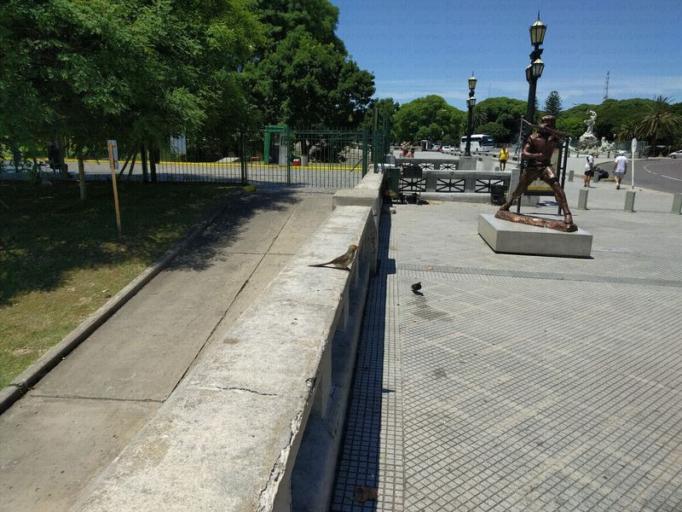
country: AR
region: Buenos Aires F.D.
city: Buenos Aires
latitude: -34.6162
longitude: -58.3567
